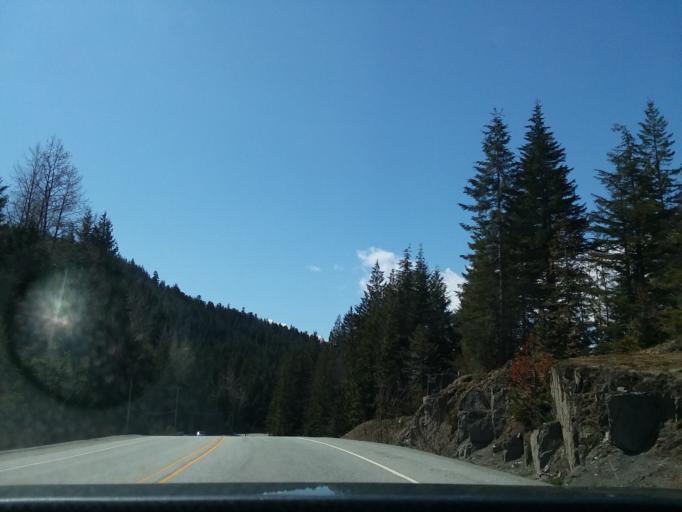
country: CA
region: British Columbia
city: Whistler
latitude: 50.0886
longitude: -123.0195
